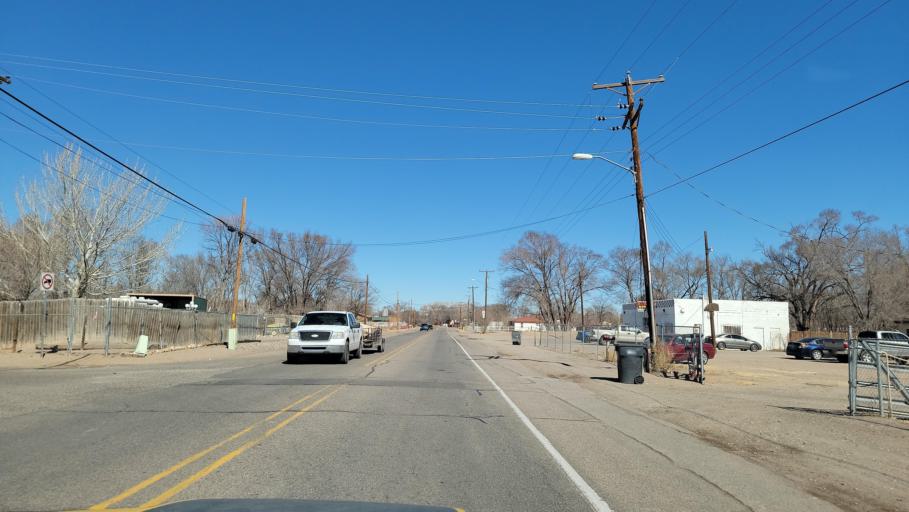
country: US
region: New Mexico
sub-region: Bernalillo County
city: South Valley
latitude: 34.9620
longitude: -106.6957
